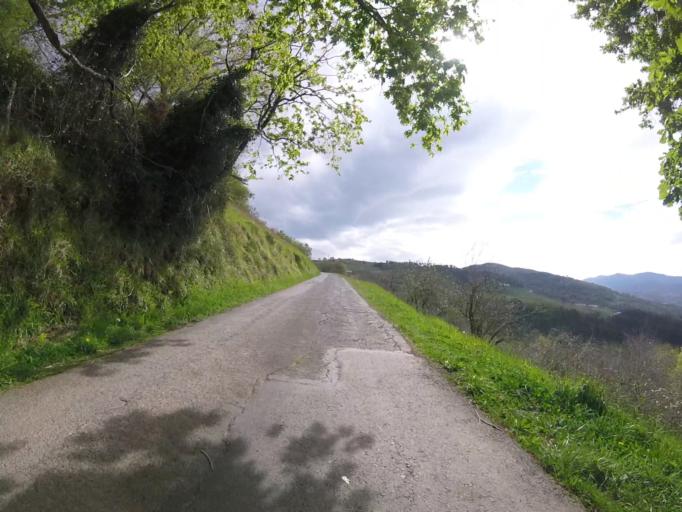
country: ES
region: Basque Country
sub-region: Provincia de Guipuzcoa
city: Aizarnazabal
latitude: 43.2511
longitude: -2.2043
